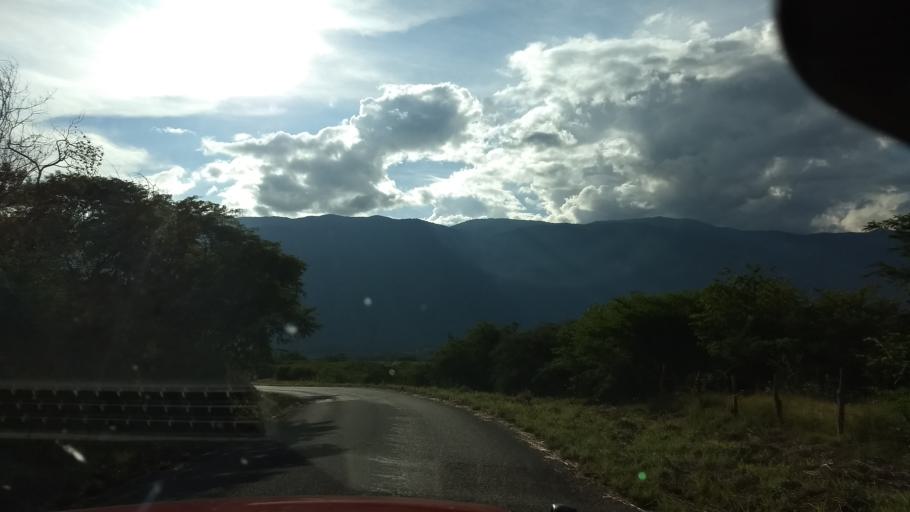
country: MX
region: Colima
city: Suchitlan
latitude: 19.4585
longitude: -103.7972
